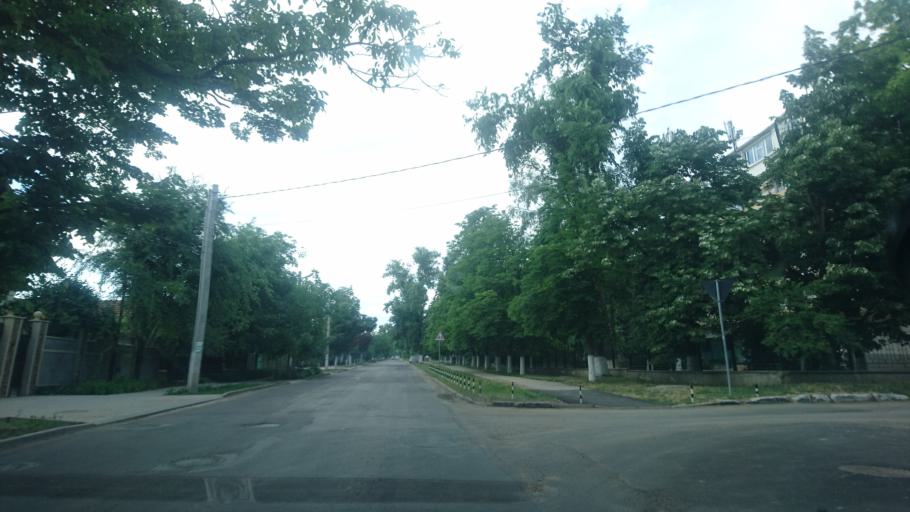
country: MD
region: Chisinau
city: Stauceni
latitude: 47.0576
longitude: 28.8393
